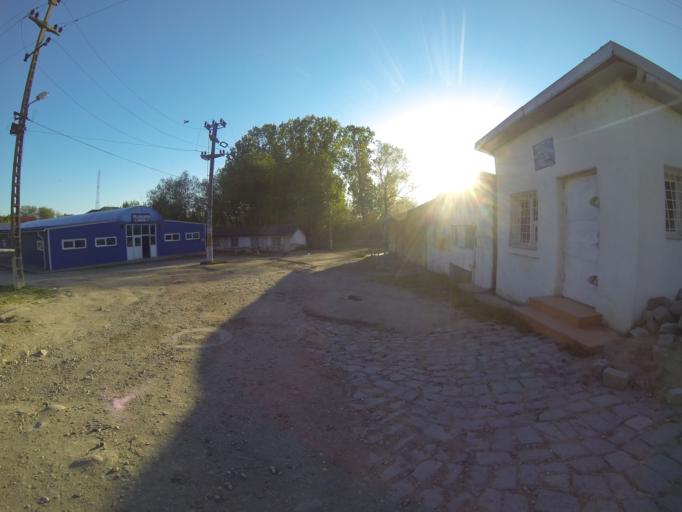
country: RO
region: Dolj
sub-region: Comuna Segarcea
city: Segarcea
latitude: 44.0950
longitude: 23.7439
